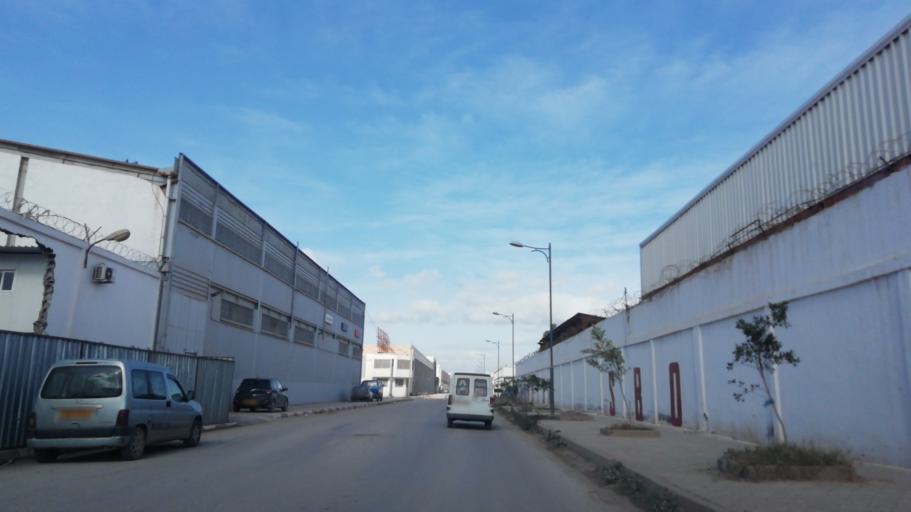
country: DZ
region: Oran
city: Es Senia
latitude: 35.6440
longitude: -0.5887
